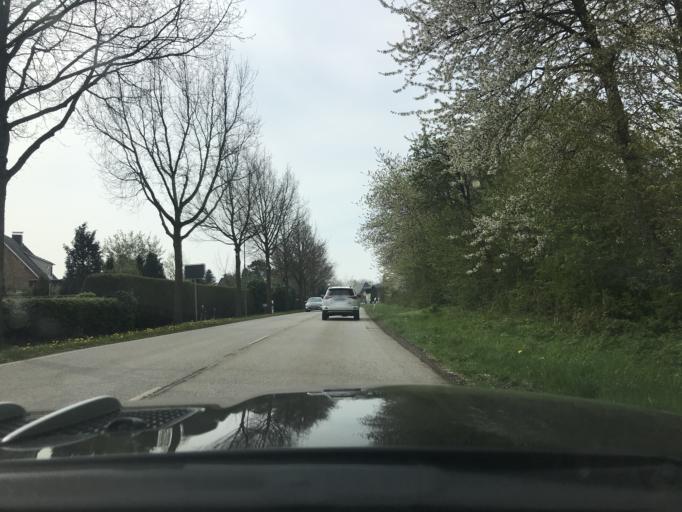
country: DE
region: Schleswig-Holstein
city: Heringsdorf
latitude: 54.2782
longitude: 11.0316
